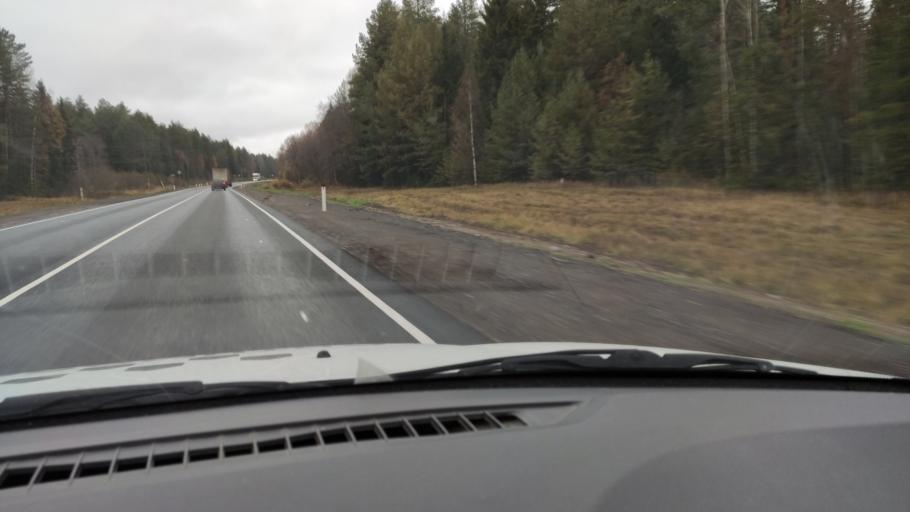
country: RU
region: Kirov
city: Belaya Kholunitsa
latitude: 58.8420
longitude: 50.7739
